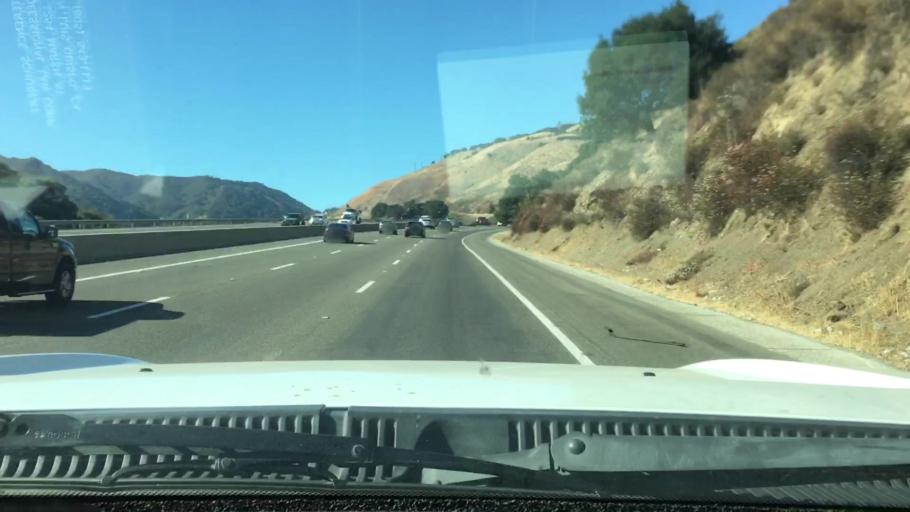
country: US
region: California
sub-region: San Luis Obispo County
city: San Luis Obispo
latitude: 35.3201
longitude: -120.6206
